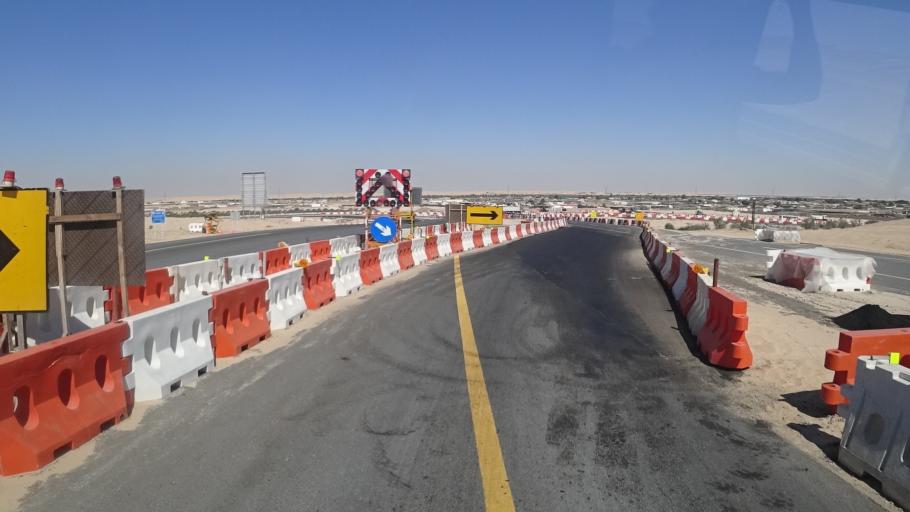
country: AE
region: Abu Dhabi
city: Abu Dhabi
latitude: 24.1998
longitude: 54.8570
